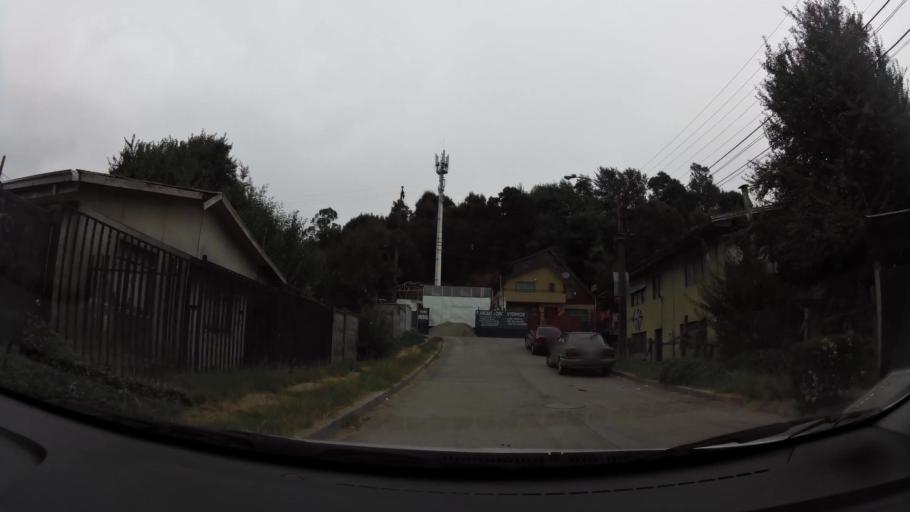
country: CL
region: Biobio
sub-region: Provincia de Concepcion
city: Concepcion
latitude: -36.8349
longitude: -73.0037
